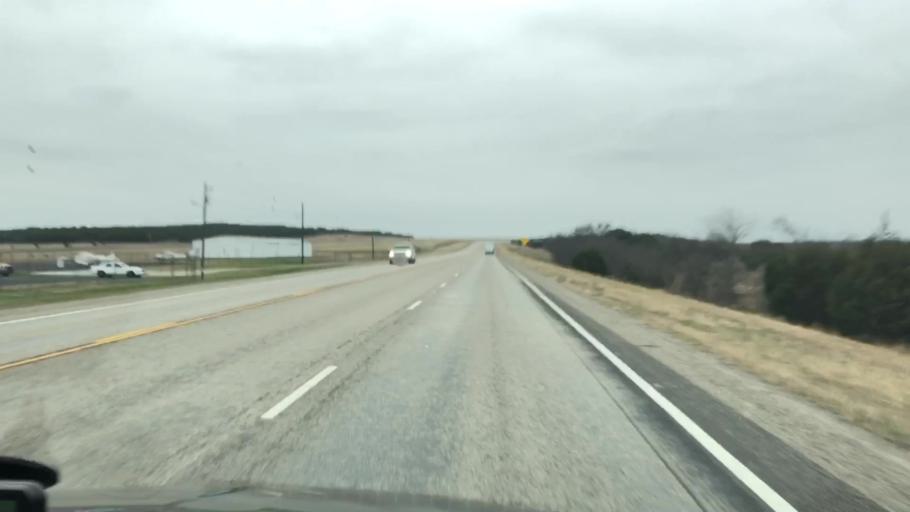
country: US
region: Texas
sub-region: Lampasas County
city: Lampasas
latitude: 31.1031
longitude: -98.1935
